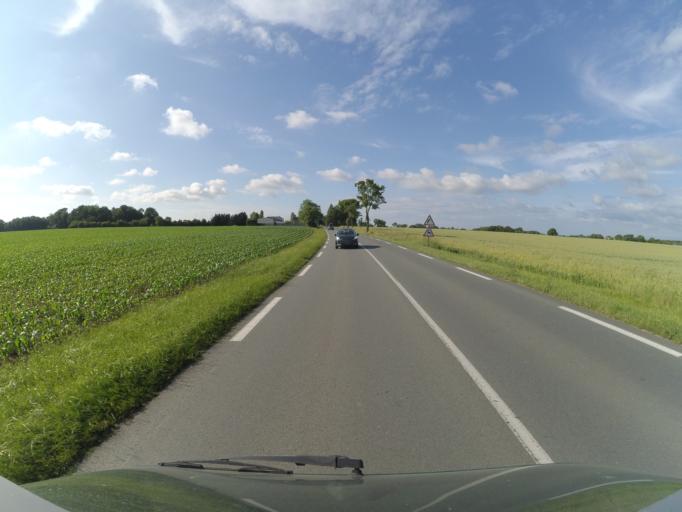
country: FR
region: Poitou-Charentes
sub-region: Departement de la Charente-Maritime
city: Le Gua
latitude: 45.7440
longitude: -0.9488
